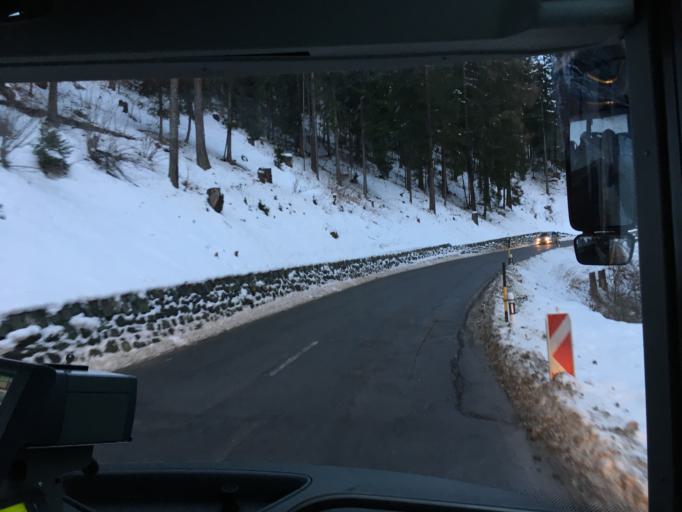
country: CH
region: Grisons
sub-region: Albula District
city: Tiefencastel
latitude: 46.5713
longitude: 9.6240
